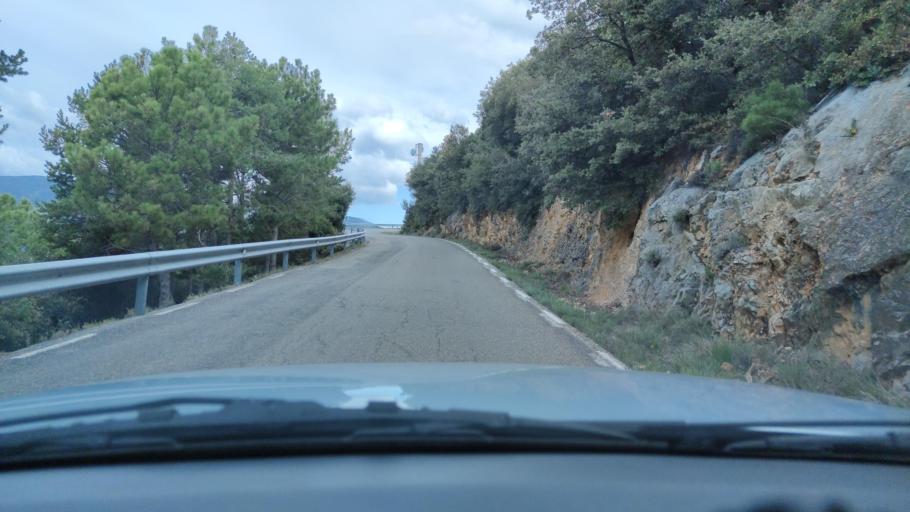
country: ES
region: Catalonia
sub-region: Provincia de Lleida
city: Coll de Nargo
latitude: 42.2495
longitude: 1.3612
